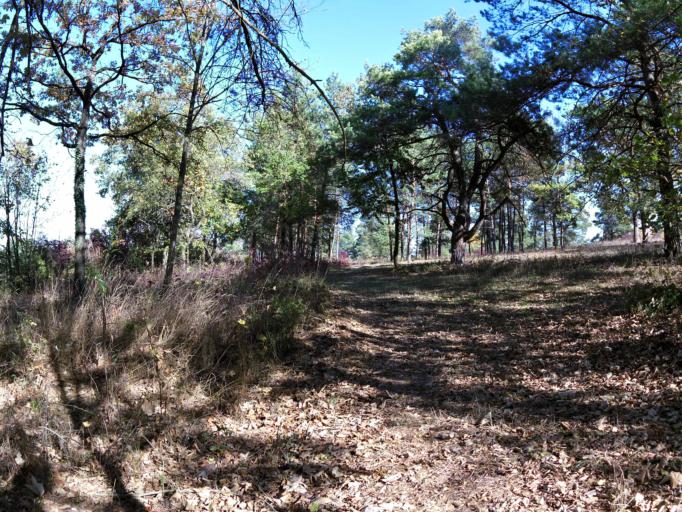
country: DE
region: Bavaria
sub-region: Regierungsbezirk Unterfranken
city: Eibelstadt
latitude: 49.7193
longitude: 9.9872
